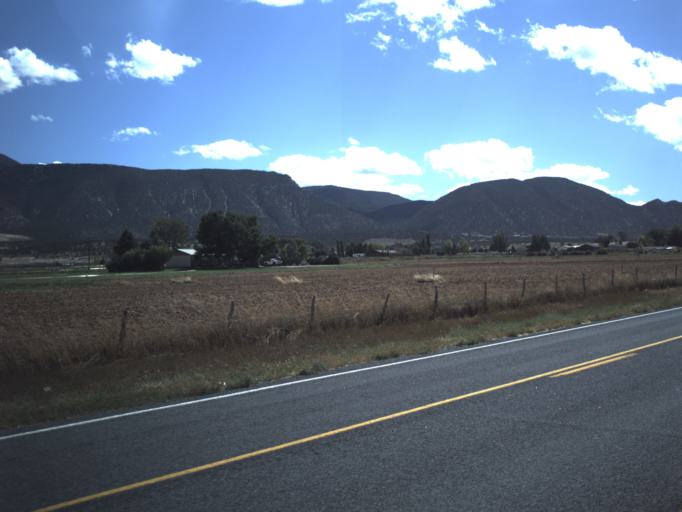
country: US
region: Utah
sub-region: Iron County
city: Enoch
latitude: 37.7465
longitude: -113.0553
